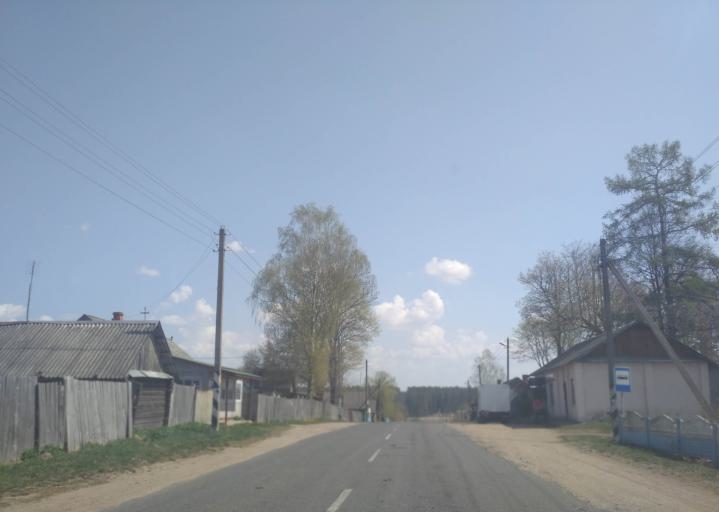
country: BY
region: Minsk
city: Loshnitsa
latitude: 54.4914
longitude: 28.6689
